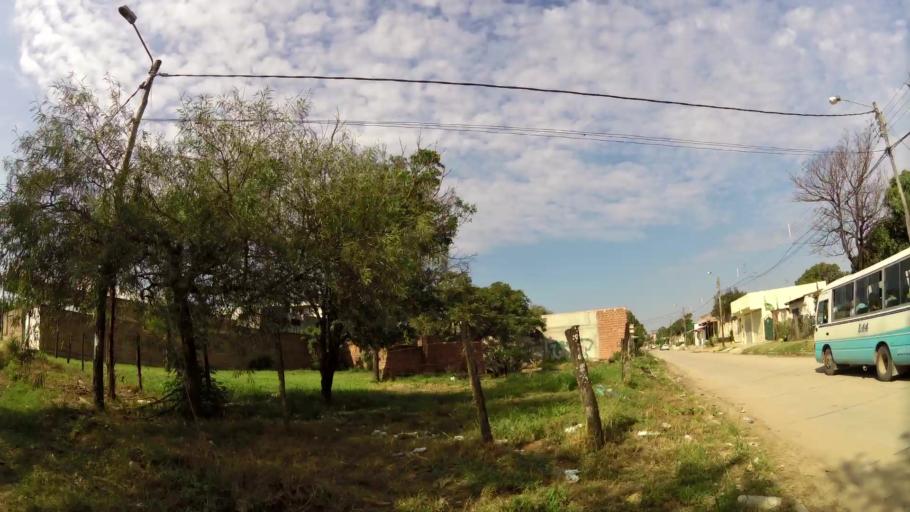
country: BO
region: Santa Cruz
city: Santa Cruz de la Sierra
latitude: -17.7324
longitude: -63.1361
